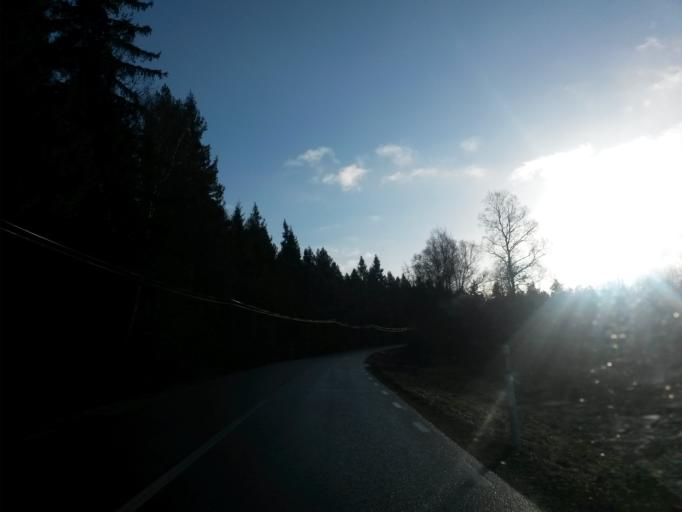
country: SE
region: Vaestra Goetaland
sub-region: Boras Kommun
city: Boras
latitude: 57.8880
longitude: 12.9287
